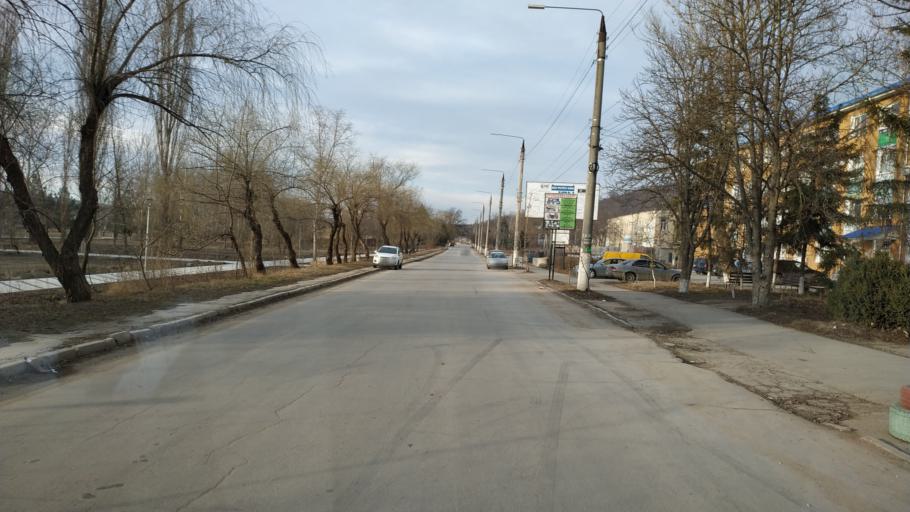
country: MD
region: Nisporeni
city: Nisporeni
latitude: 47.0830
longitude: 28.1825
